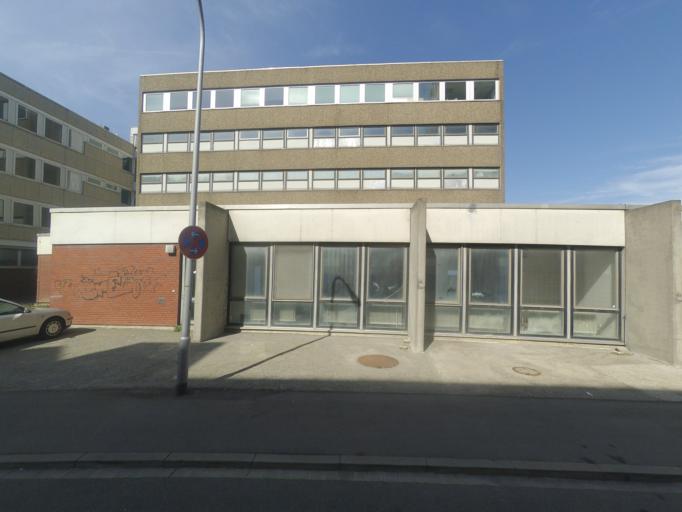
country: DE
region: Baden-Wuerttemberg
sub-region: Karlsruhe Region
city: Mannheim
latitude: 49.5105
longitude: 8.4560
